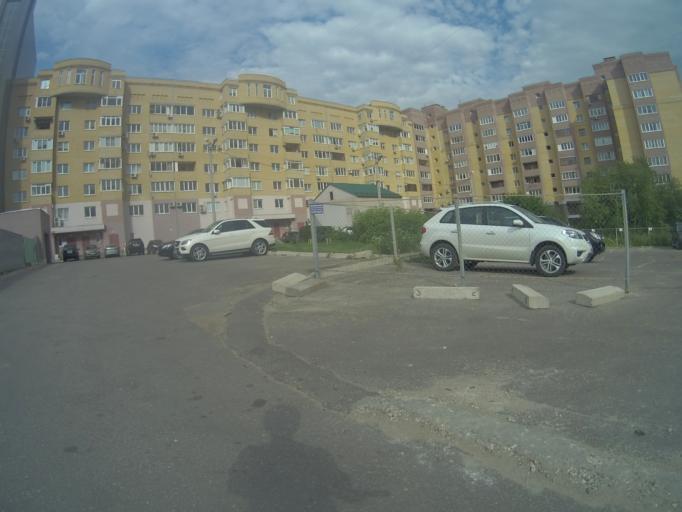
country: RU
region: Vladimir
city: Vladimir
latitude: 56.1368
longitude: 40.3995
